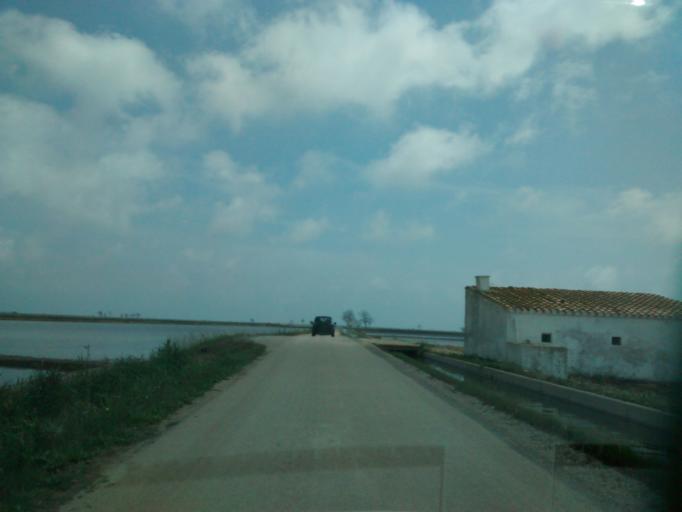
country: ES
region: Catalonia
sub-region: Provincia de Tarragona
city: Deltebre
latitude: 40.6839
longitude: 0.7905
